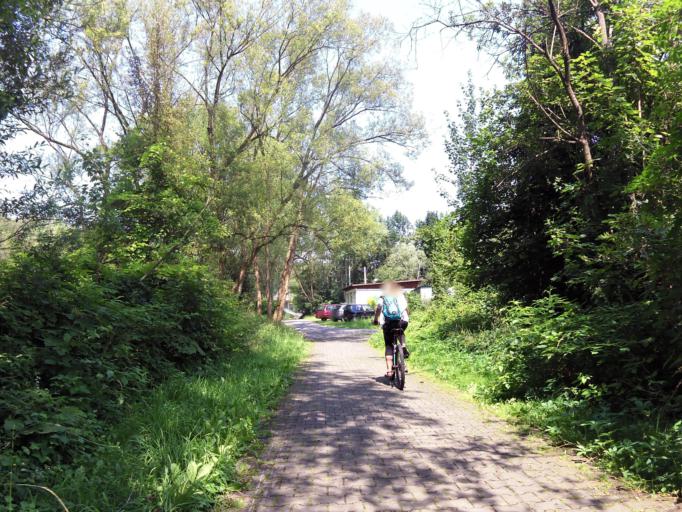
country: PL
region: Silesian Voivodeship
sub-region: Powiat zywiecki
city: Milowka
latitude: 49.5593
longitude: 19.0826
